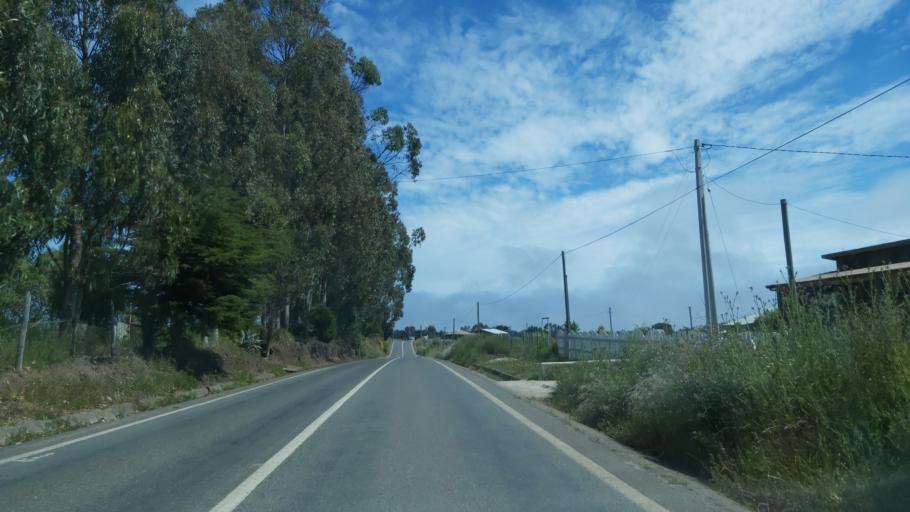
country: CL
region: Maule
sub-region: Provincia de Talca
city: Constitucion
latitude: -35.5797
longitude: -72.6012
